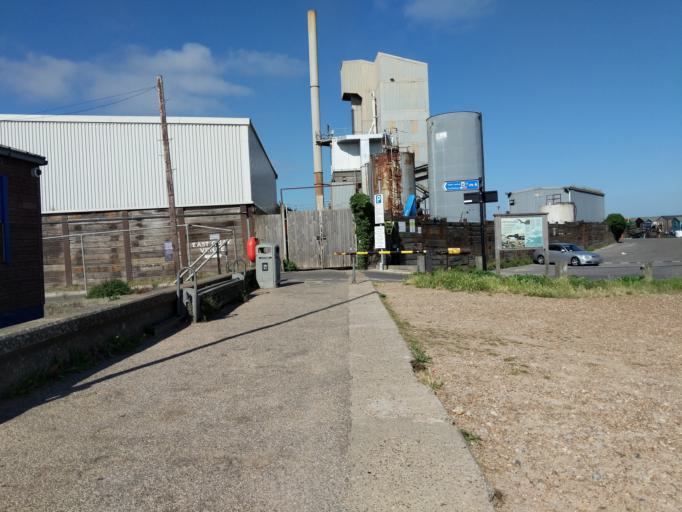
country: GB
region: England
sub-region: Kent
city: Whitstable
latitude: 51.3640
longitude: 1.0288
